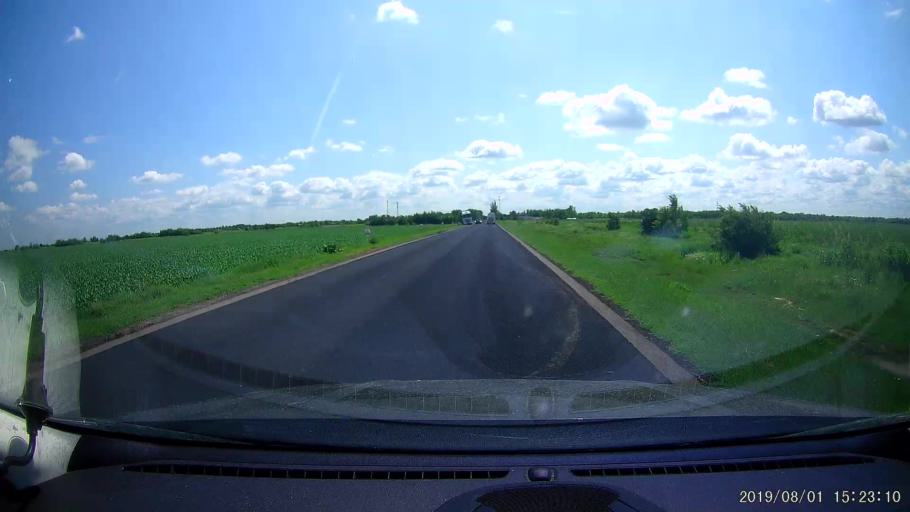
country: RO
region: Braila
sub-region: Comuna Viziru
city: Lanurile
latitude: 45.0439
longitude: 27.7638
